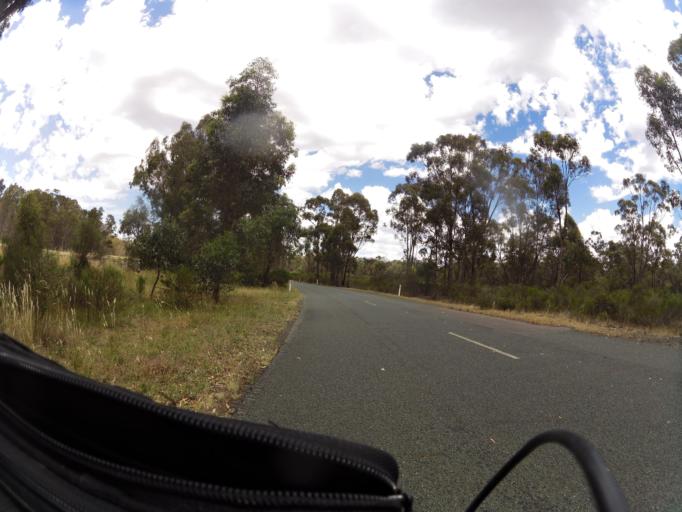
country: AU
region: Victoria
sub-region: Greater Shepparton
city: Shepparton
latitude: -36.6855
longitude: 145.1810
